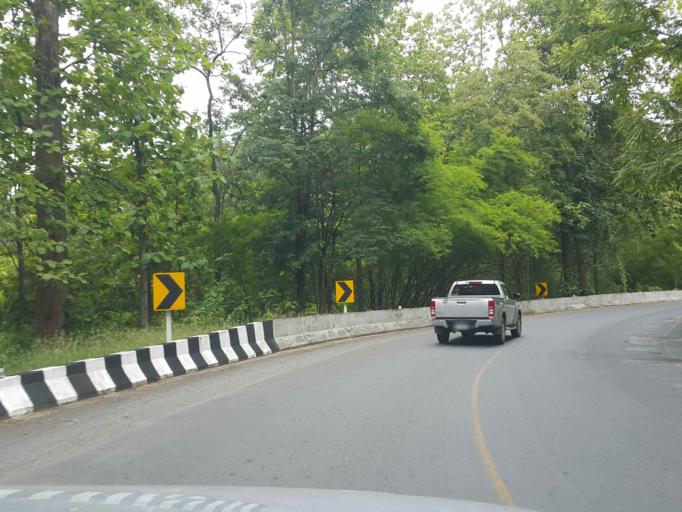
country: TH
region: Lampang
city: Thoen
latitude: 17.6177
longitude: 99.3205
